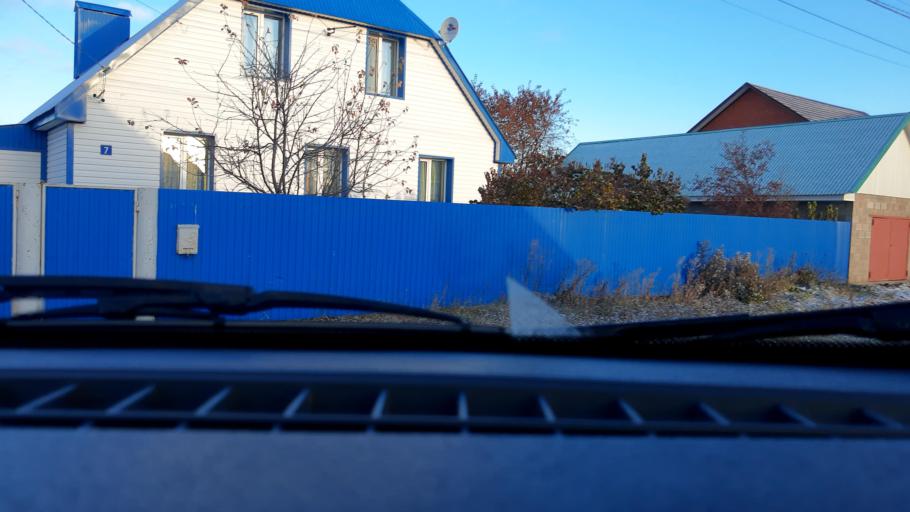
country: RU
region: Bashkortostan
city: Mikhaylovka
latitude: 54.7901
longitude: 55.8263
